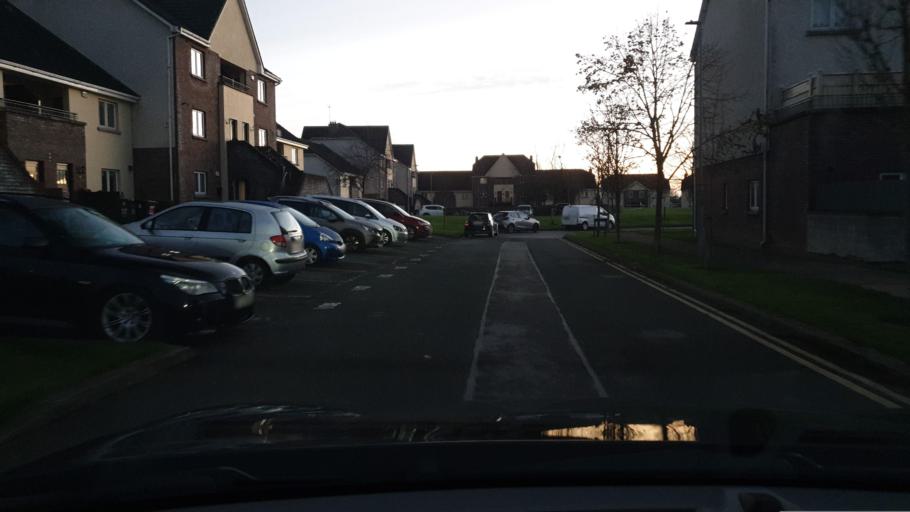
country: IE
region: Leinster
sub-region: An Mhi
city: Ashbourne
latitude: 53.5139
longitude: -6.4062
